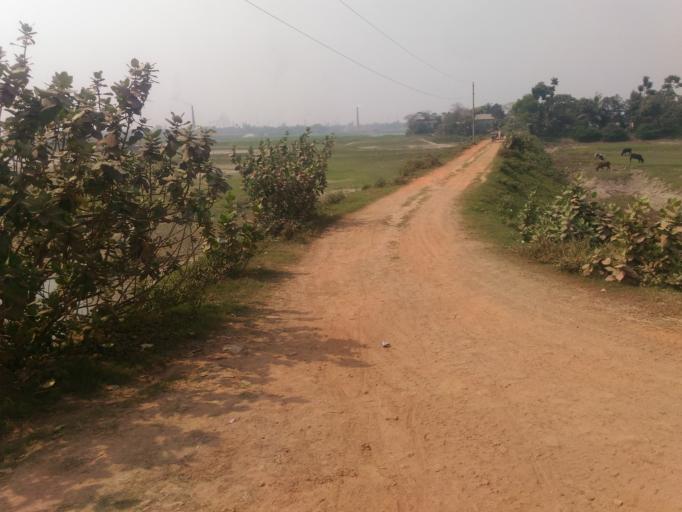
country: BD
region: Dhaka
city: Narayanganj
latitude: 23.6397
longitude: 90.4510
